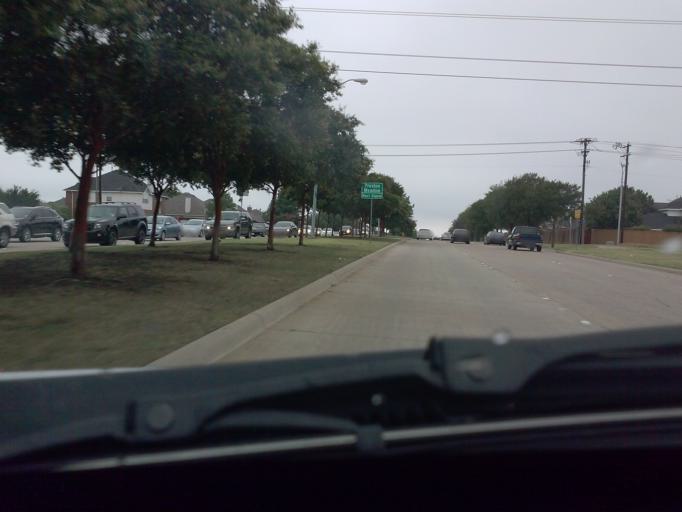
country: US
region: Texas
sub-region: Collin County
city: Plano
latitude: 33.0563
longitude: -96.7760
